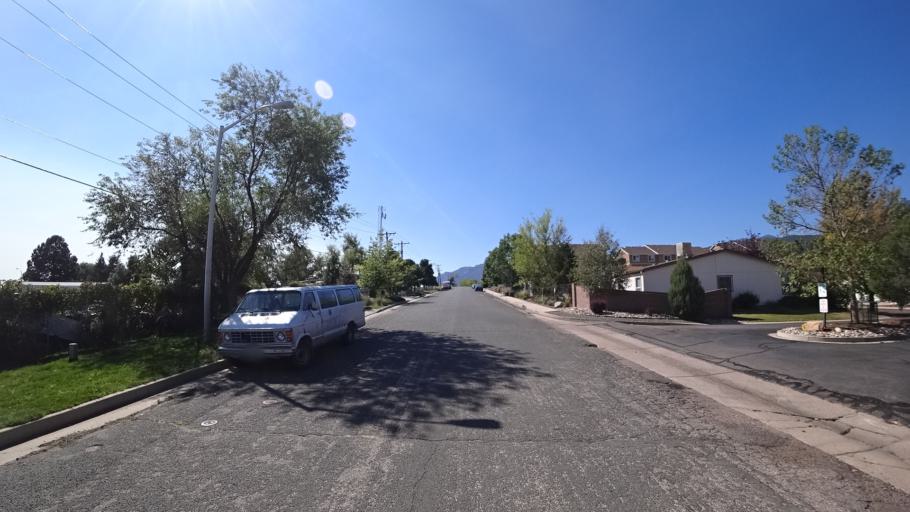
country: US
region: Colorado
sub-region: El Paso County
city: Colorado Springs
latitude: 38.8314
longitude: -104.8606
